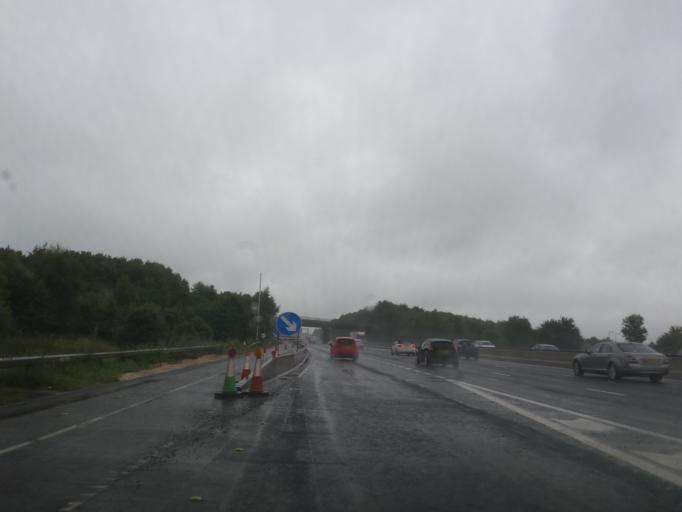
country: GB
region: England
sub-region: Derbyshire
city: Tibshelf
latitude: 53.1377
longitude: -1.3306
